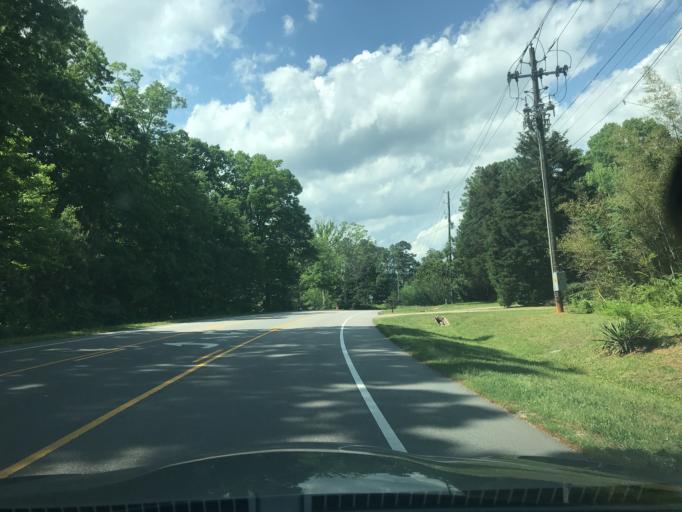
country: US
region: North Carolina
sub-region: Wake County
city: West Raleigh
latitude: 35.8837
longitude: -78.5999
